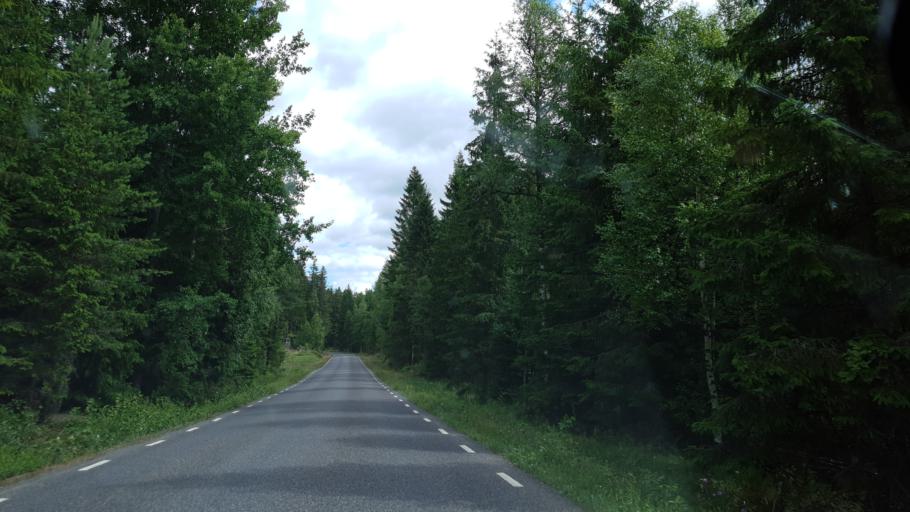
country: SE
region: Kronoberg
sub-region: Uppvidinge Kommun
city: Aseda
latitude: 57.1887
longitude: 15.3893
